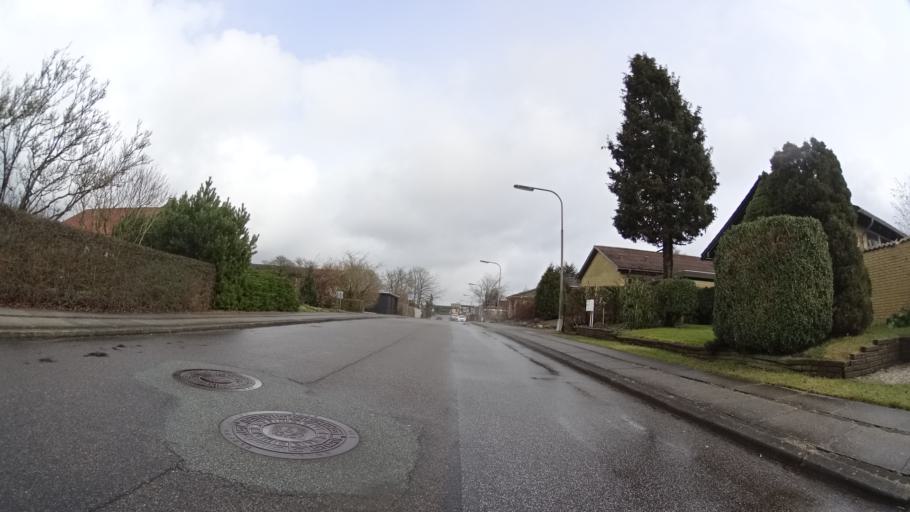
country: DK
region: Central Jutland
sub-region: Arhus Kommune
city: Arhus
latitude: 56.1722
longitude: 10.1621
